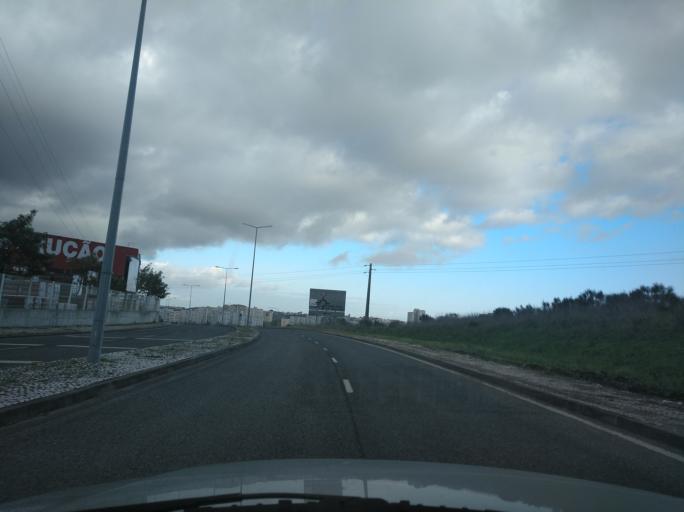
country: PT
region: Lisbon
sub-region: Loures
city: Loures
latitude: 38.8166
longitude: -9.1771
